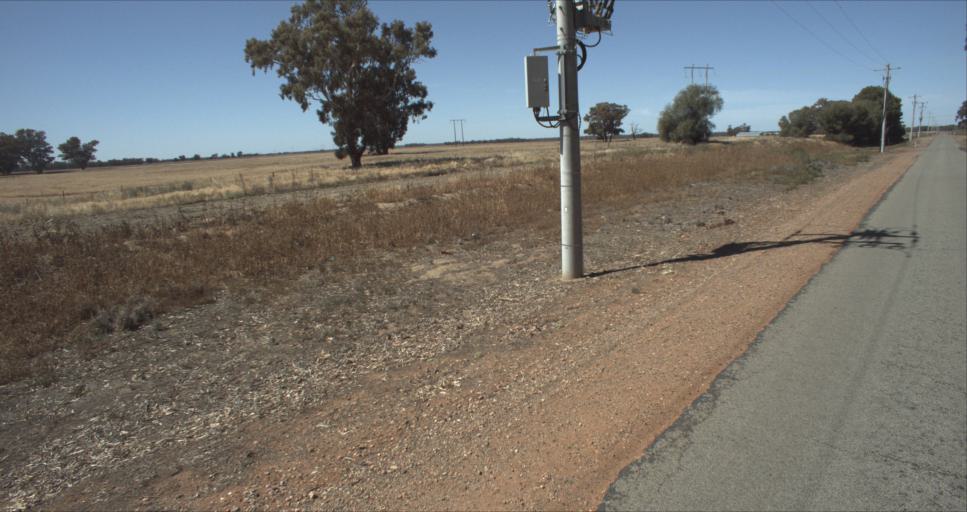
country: AU
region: New South Wales
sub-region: Leeton
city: Leeton
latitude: -34.5736
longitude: 146.3101
